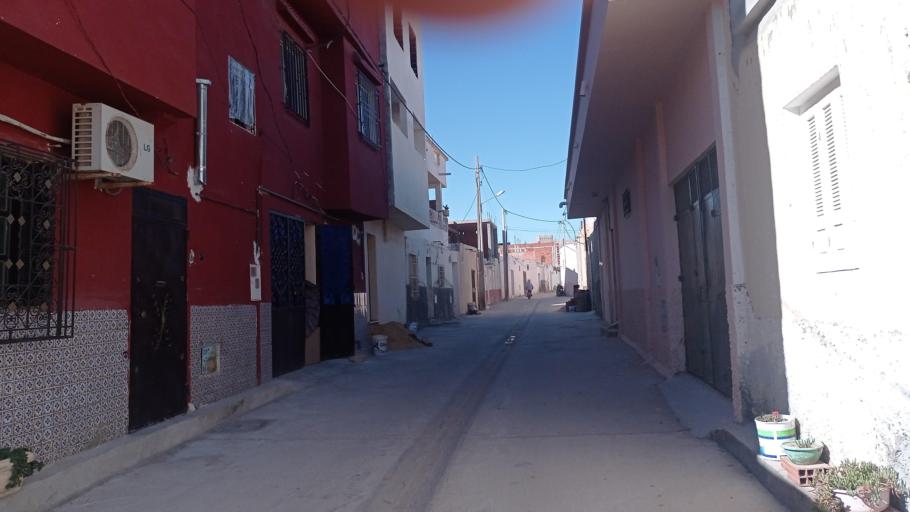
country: TN
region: Qabis
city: Gabes
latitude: 33.8424
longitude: 10.1168
